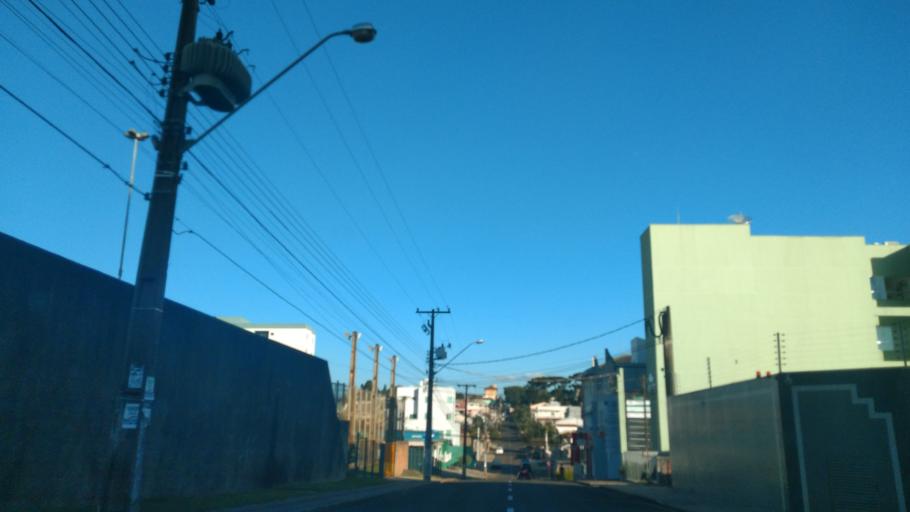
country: BR
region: Parana
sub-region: Guarapuava
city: Guarapuava
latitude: -25.3979
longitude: -51.4650
